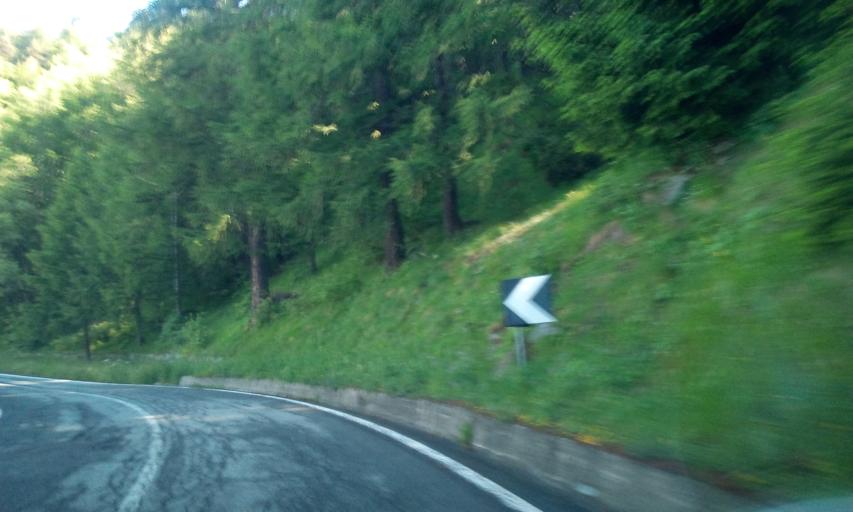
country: IT
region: Aosta Valley
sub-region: Valle d'Aosta
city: Emarese
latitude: 45.7505
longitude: 7.6948
